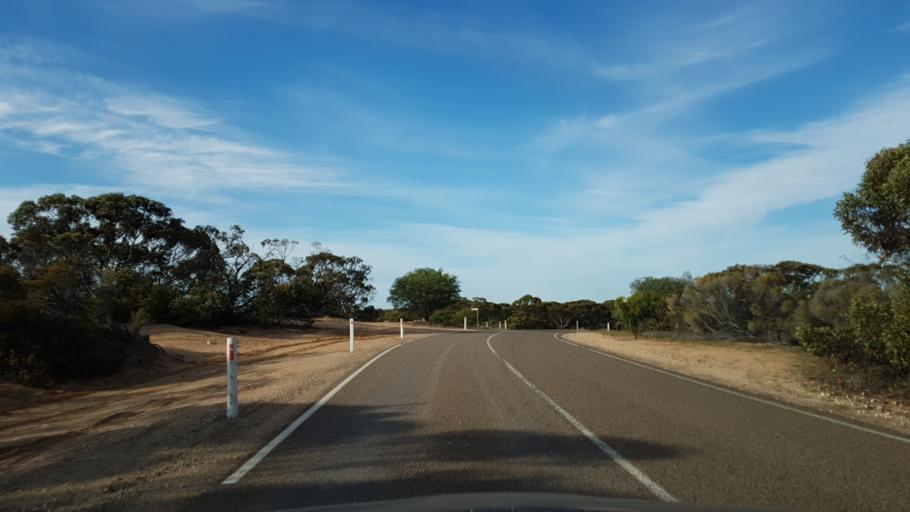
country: AU
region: South Australia
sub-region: Murray Bridge
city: Murray Bridge
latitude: -35.0435
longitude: 139.4651
